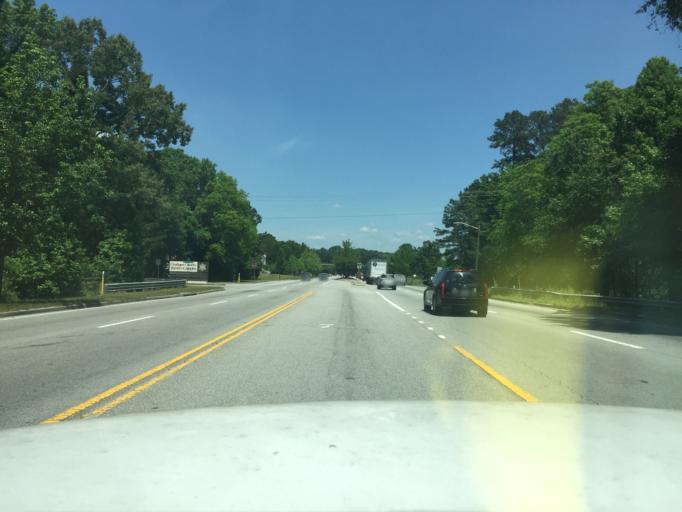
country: US
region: Georgia
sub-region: Chatham County
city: Garden City
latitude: 32.0603
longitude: -81.1607
